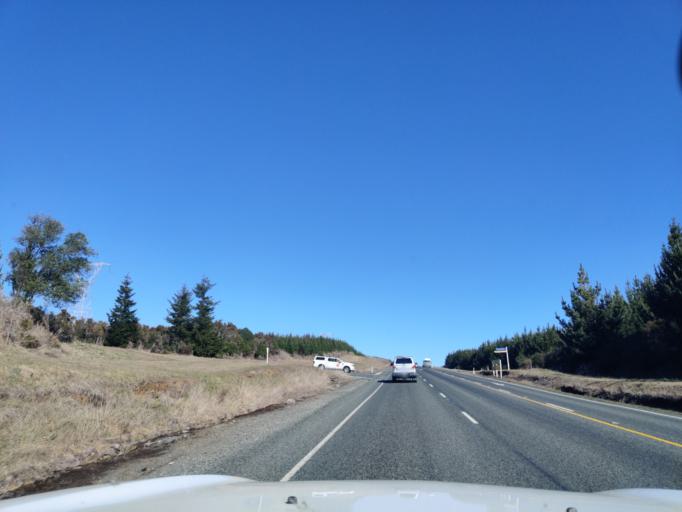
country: NZ
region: Waikato
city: Turangi
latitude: -39.1159
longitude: 175.8028
